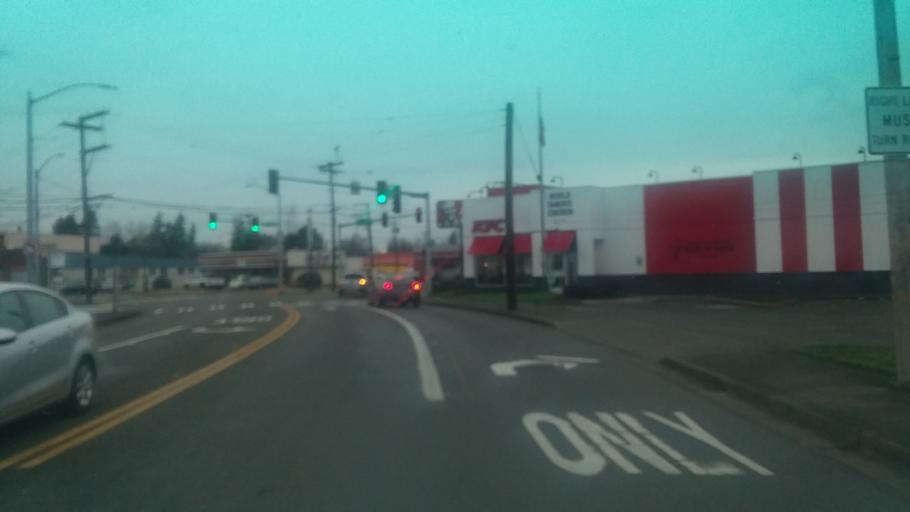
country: US
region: Washington
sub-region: Pierce County
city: Puyallup
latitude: 47.1926
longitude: -122.2916
